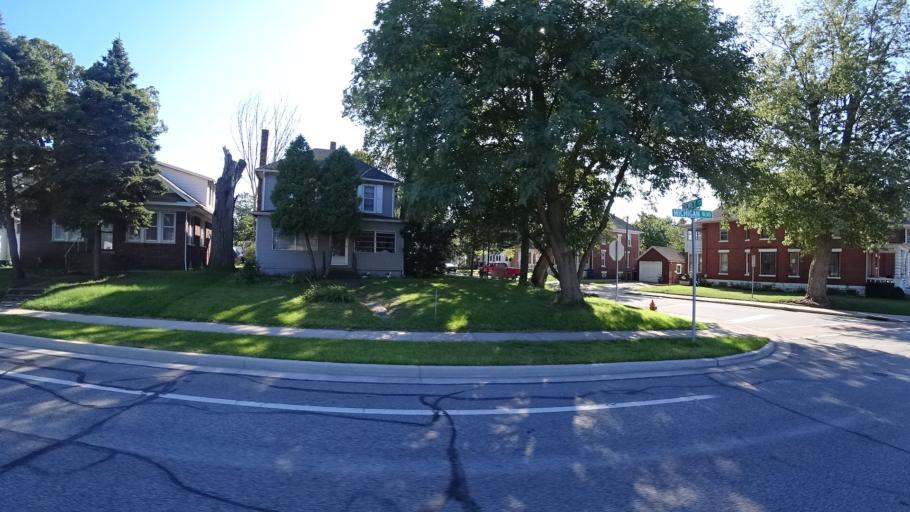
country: US
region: Indiana
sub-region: LaPorte County
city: Michigan City
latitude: 41.7103
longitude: -86.8760
